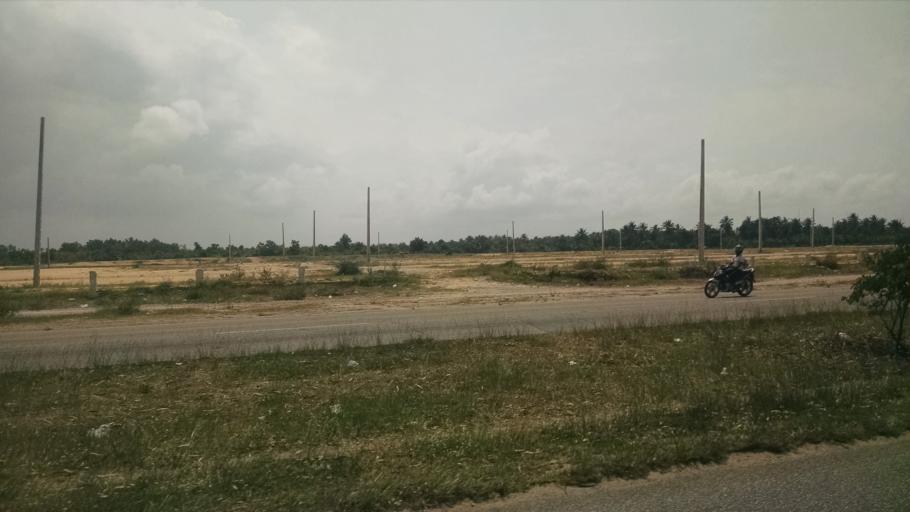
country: CI
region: Lagunes
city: Abidjan
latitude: 5.2624
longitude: -3.9478
